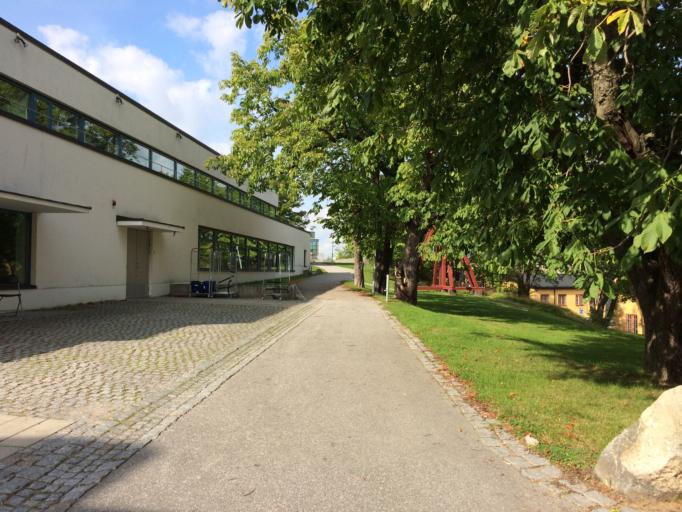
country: SE
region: Stockholm
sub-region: Stockholms Kommun
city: OEstermalm
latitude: 59.3255
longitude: 18.0862
